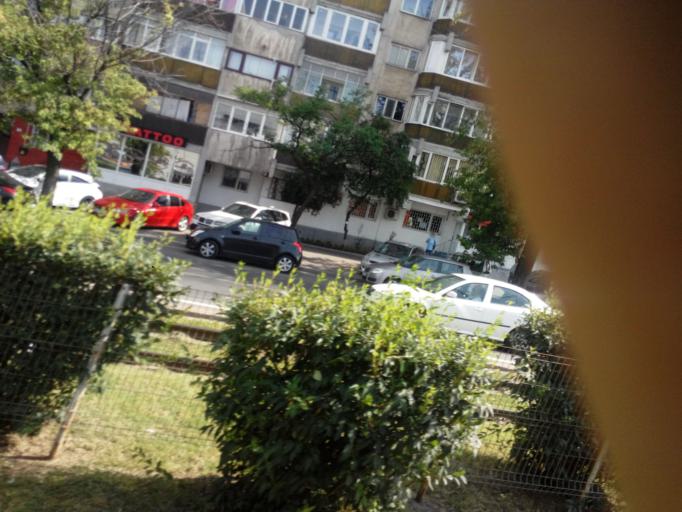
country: RO
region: Ilfov
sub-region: Comuna Chiajna
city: Rosu
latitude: 44.4281
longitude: 26.0366
